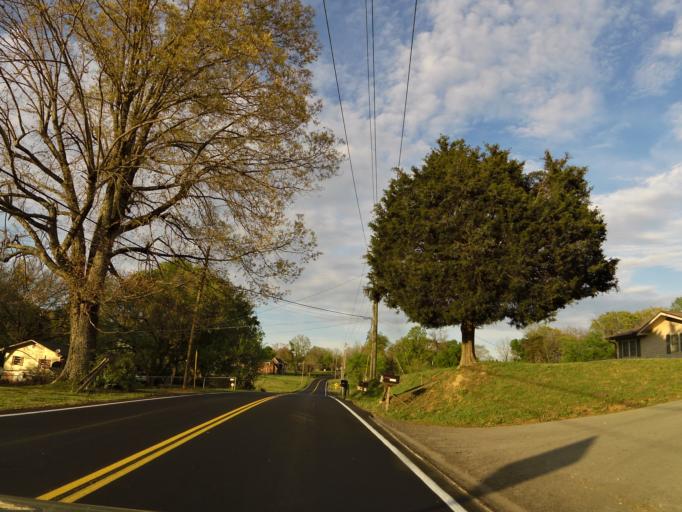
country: US
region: Tennessee
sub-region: Loudon County
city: Greenback
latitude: 35.6406
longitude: -84.0760
